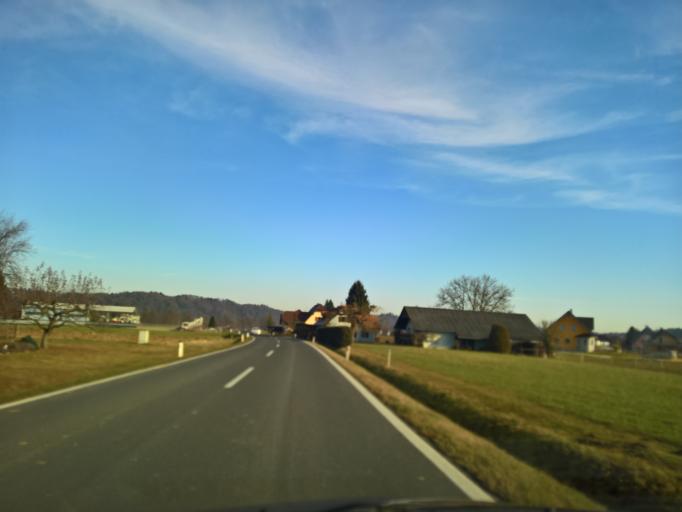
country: AT
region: Styria
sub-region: Politischer Bezirk Deutschlandsberg
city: Pitschgau
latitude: 46.6976
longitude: 15.2839
